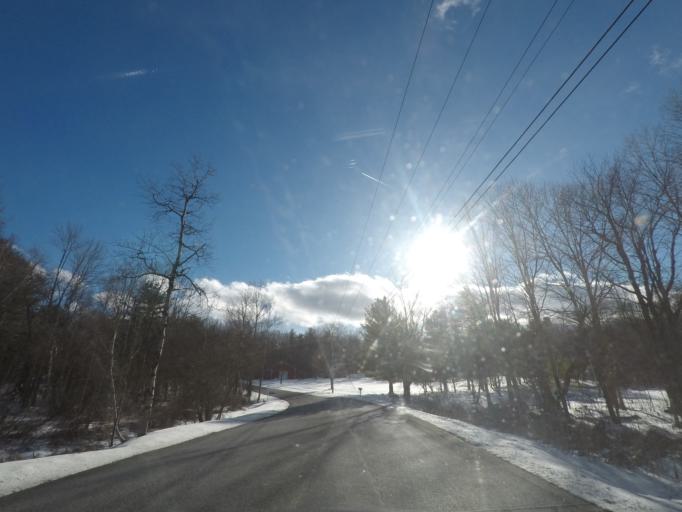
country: US
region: New York
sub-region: Rensselaer County
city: Hoosick Falls
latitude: 42.7977
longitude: -73.4004
